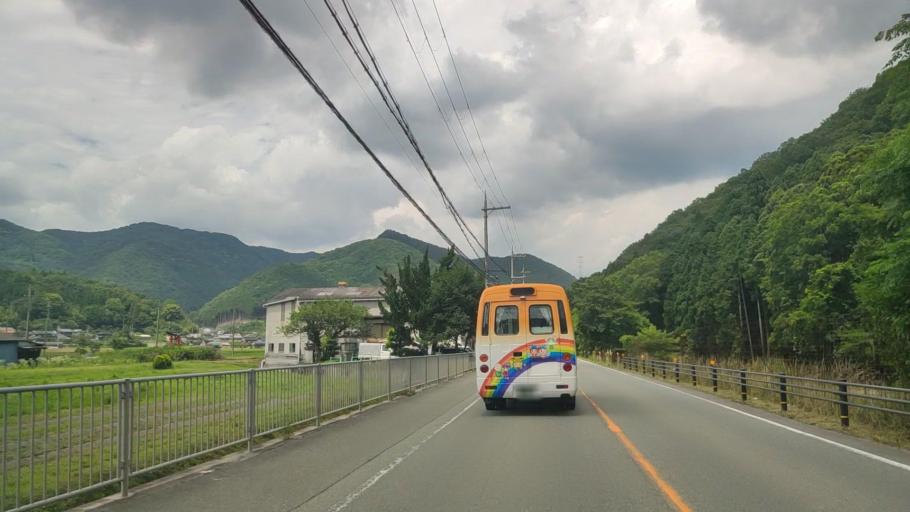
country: JP
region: Hyogo
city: Yamazakicho-nakabirose
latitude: 34.9381
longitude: 134.4837
